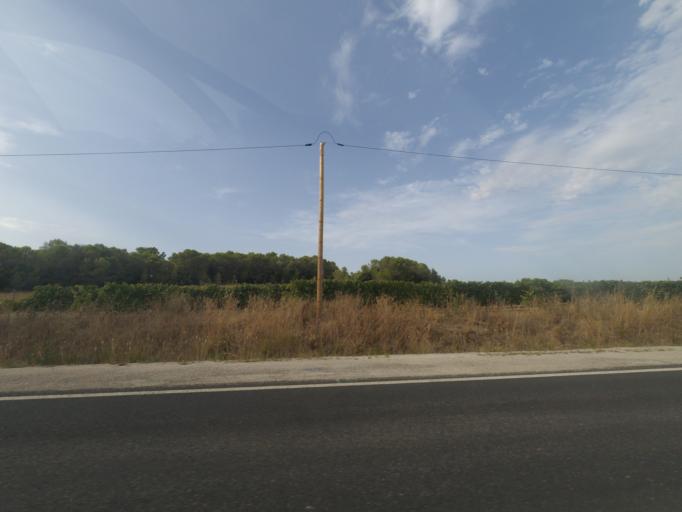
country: FR
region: Languedoc-Roussillon
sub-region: Departement de l'Herault
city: Saint-Mathieu-de-Treviers
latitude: 43.7401
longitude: 3.8439
